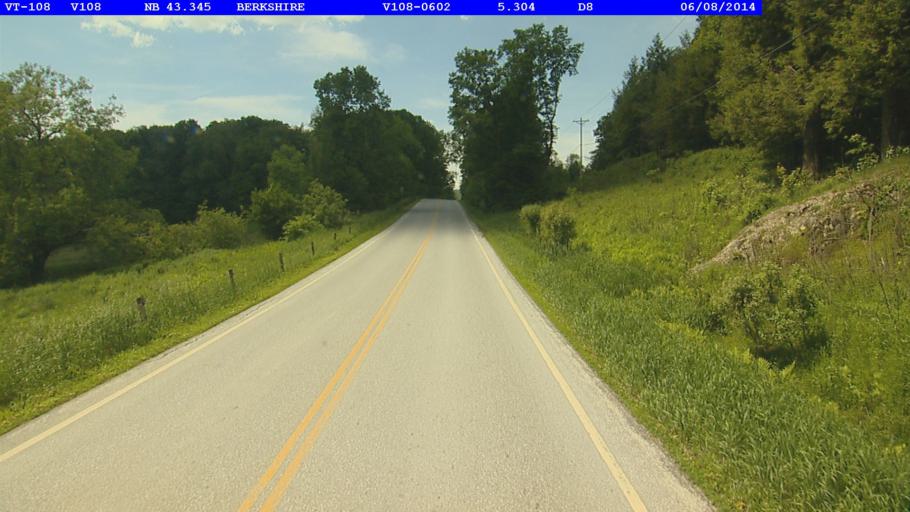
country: US
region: Vermont
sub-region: Franklin County
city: Enosburg Falls
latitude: 44.9949
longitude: -72.8192
